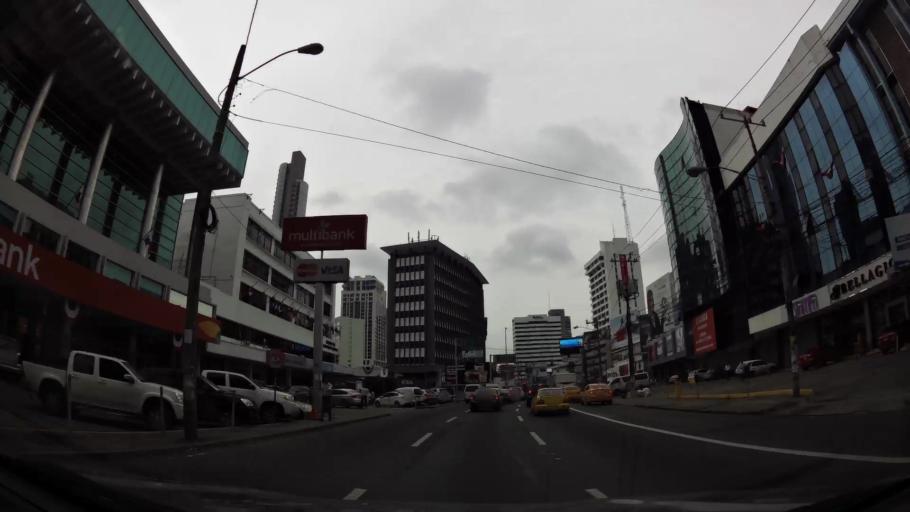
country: PA
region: Panama
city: Panama
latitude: 8.9865
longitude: -79.5238
